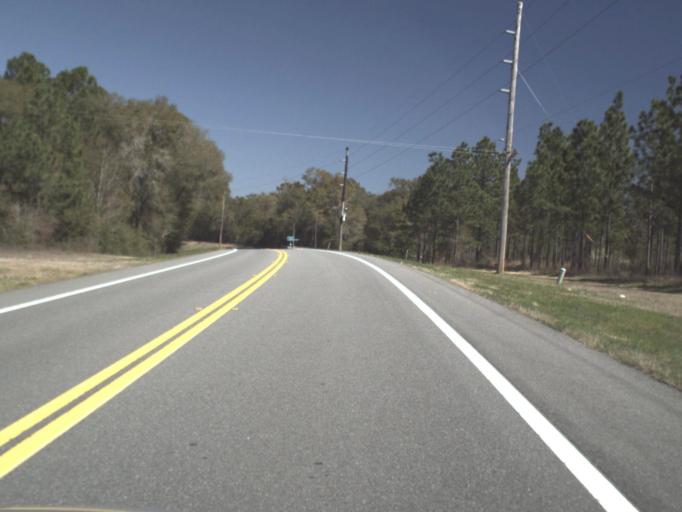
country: US
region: Florida
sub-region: Gadsden County
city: Quincy
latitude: 30.4193
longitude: -84.6498
